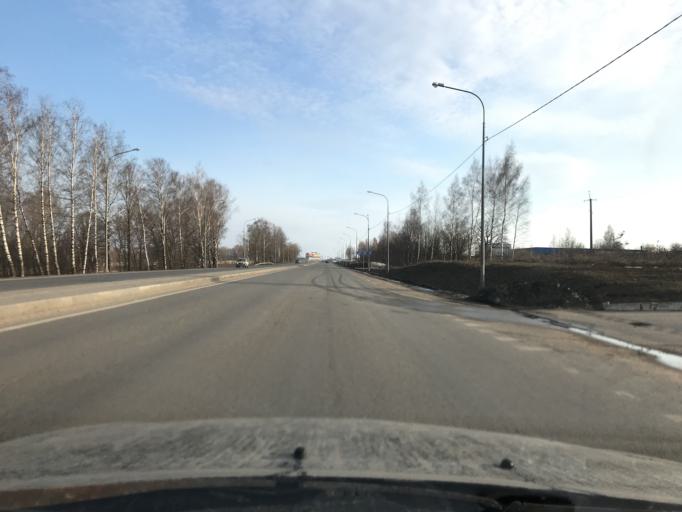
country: RU
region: Kaluga
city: Kaluga
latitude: 54.4878
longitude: 36.2297
